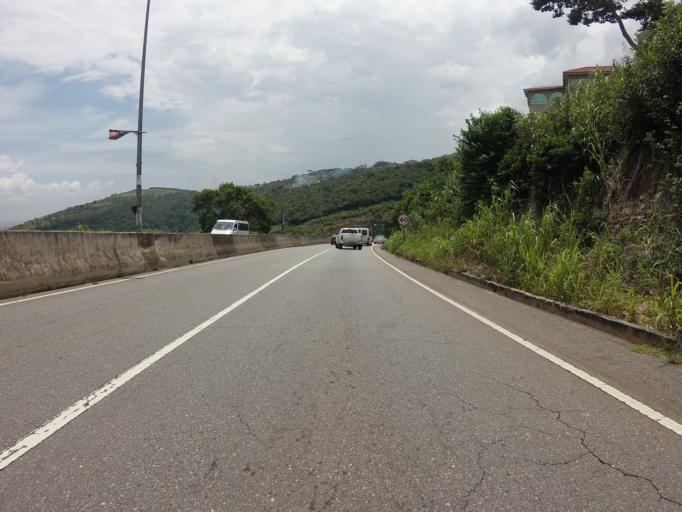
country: GH
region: Eastern
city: Aburi
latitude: 5.7950
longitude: -0.1847
